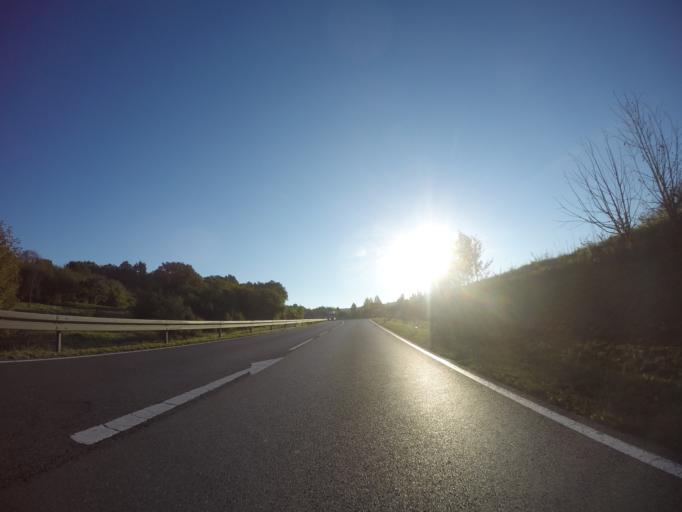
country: DE
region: Bavaria
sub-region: Regierungsbezirk Unterfranken
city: Kreuzwertheim
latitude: 49.7702
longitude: 9.5153
